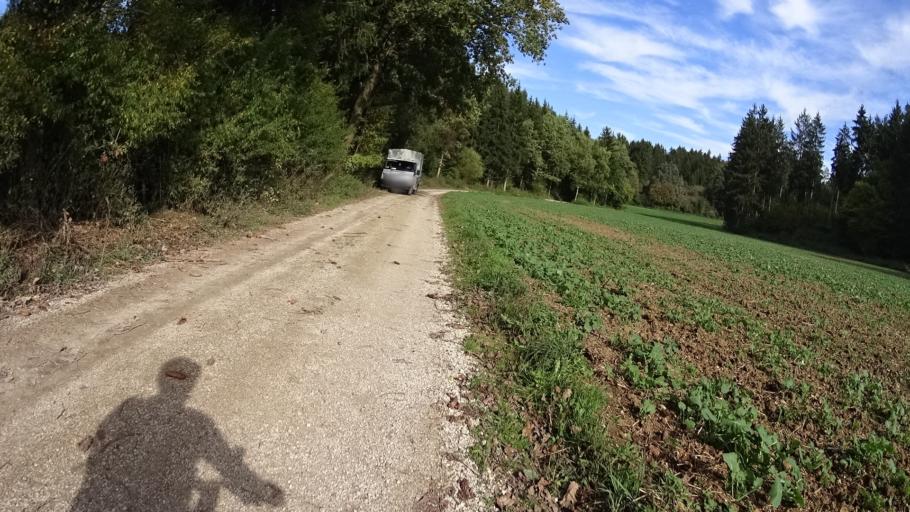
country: DE
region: Bavaria
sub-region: Upper Bavaria
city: Bohmfeld
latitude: 48.8699
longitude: 11.3704
